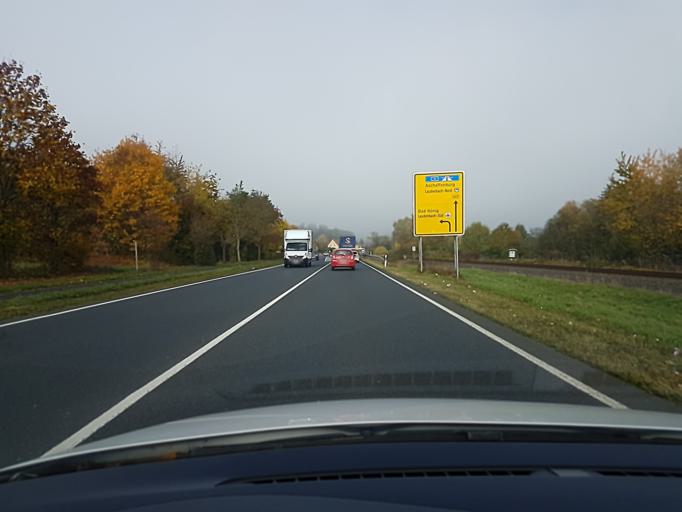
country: DE
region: Bavaria
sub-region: Regierungsbezirk Unterfranken
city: Laudenbach
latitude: 49.7366
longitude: 9.1845
